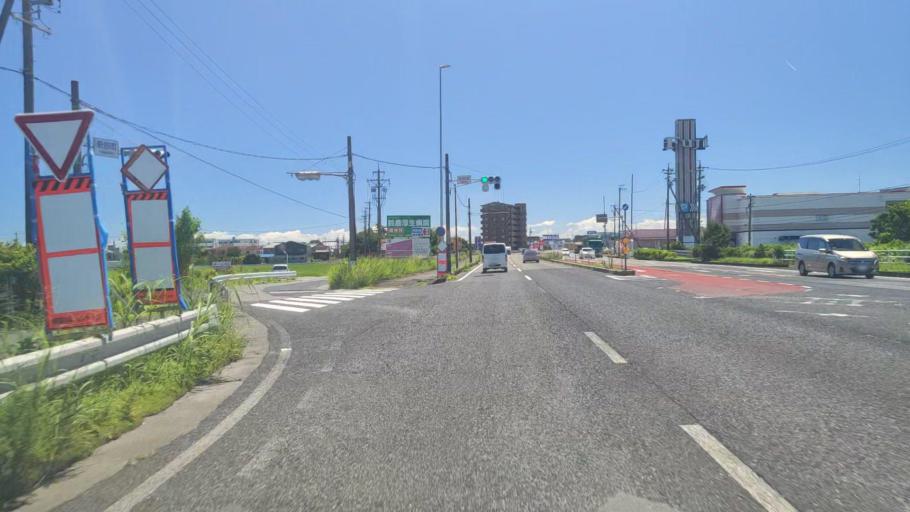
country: JP
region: Mie
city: Suzuka
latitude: 34.8689
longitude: 136.5902
